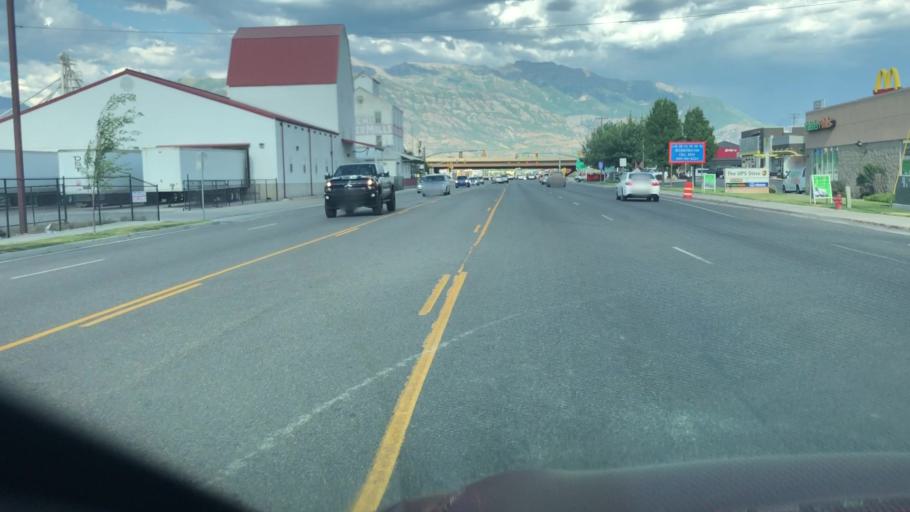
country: US
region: Utah
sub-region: Utah County
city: Lehi
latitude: 40.3883
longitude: -111.8377
